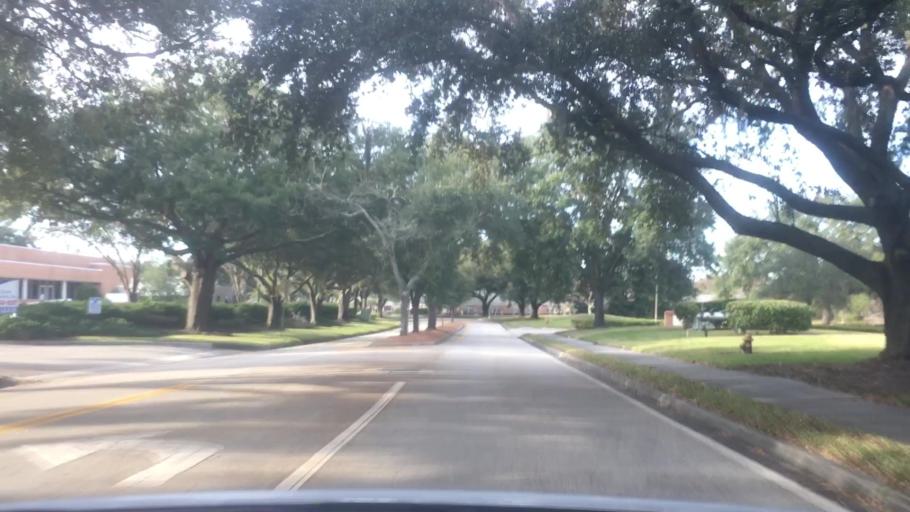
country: US
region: Florida
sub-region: Duval County
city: Jacksonville
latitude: 30.2573
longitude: -81.5864
